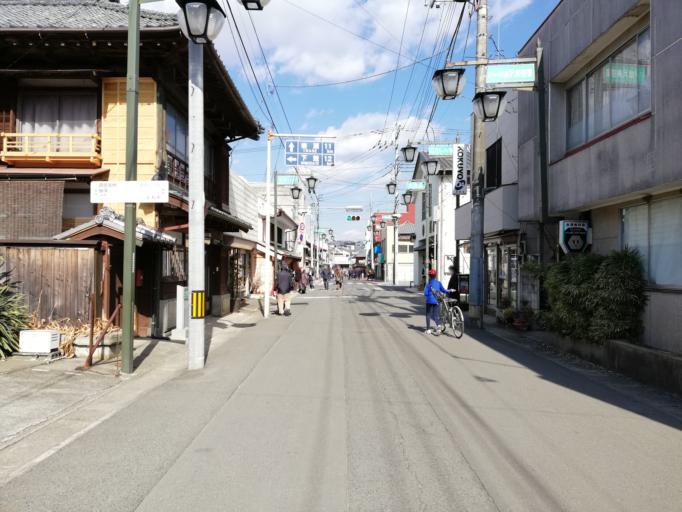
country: JP
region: Ibaraki
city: Makabe
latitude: 36.2777
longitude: 140.0994
